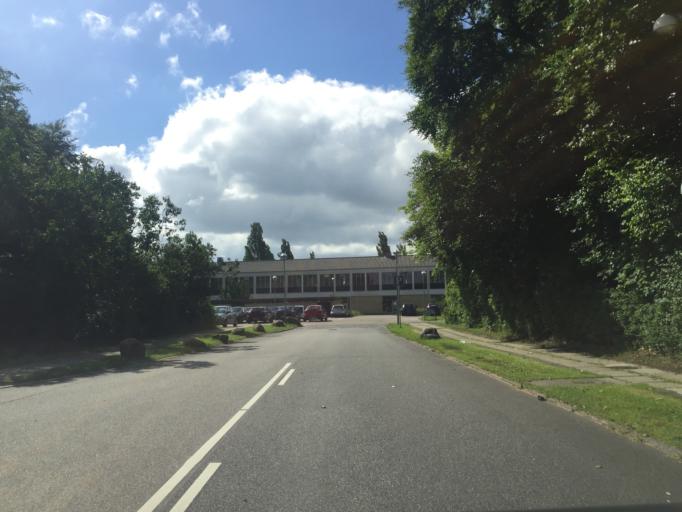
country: DK
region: Capital Region
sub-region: Brondby Kommune
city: Brondbyvester
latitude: 55.6549
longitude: 12.4193
